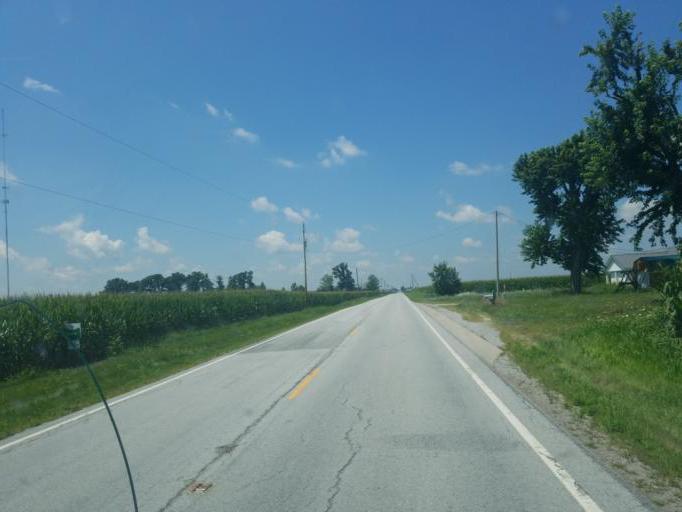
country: US
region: Ohio
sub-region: Allen County
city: Spencerville
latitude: 40.7141
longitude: -84.3788
